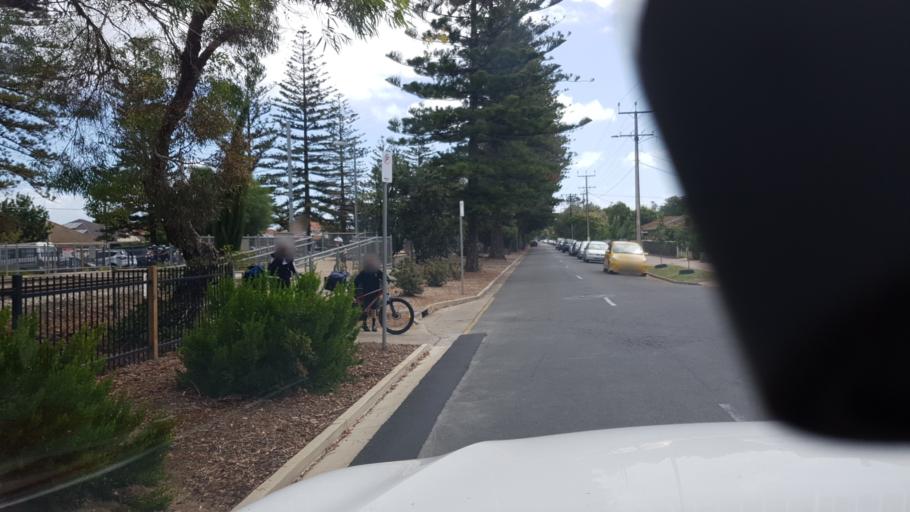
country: AU
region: South Australia
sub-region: Holdfast Bay
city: Glenelg East
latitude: -34.9796
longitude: 138.5260
